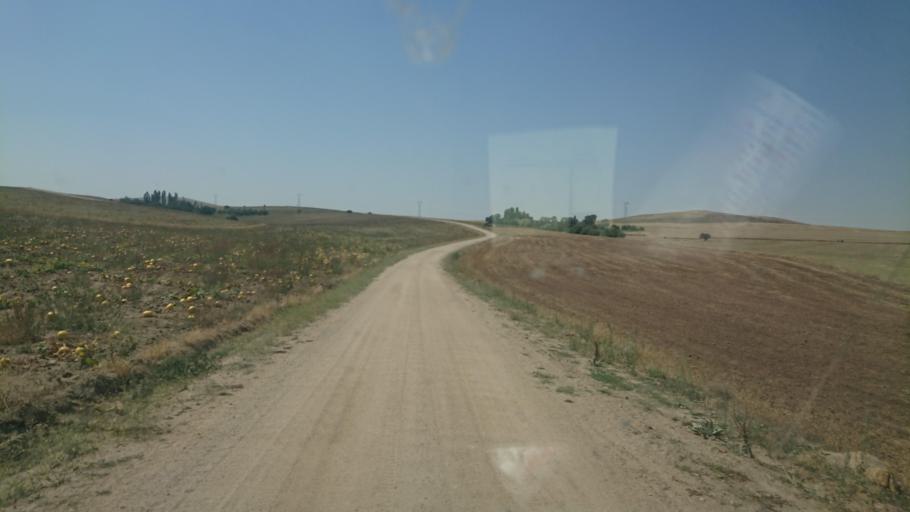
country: TR
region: Aksaray
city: Agacoren
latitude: 38.8103
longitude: 33.9521
